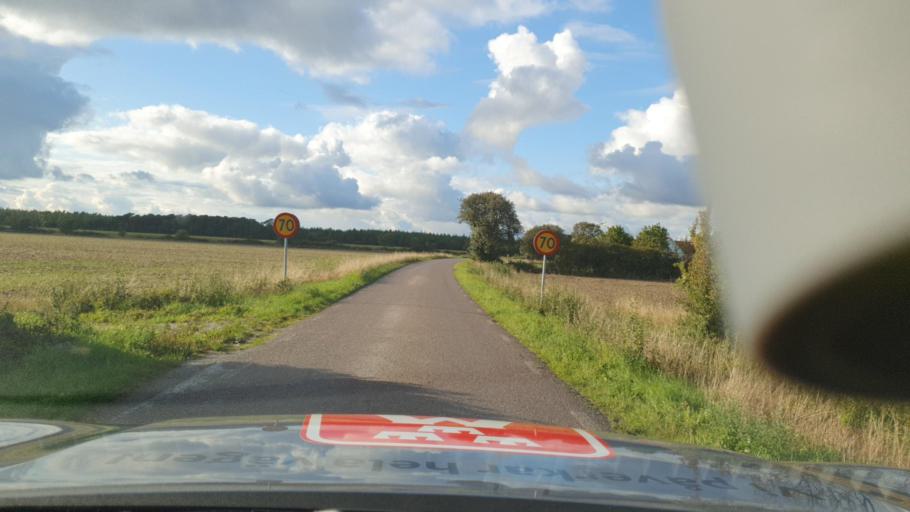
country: SE
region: Gotland
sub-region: Gotland
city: Hemse
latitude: 57.1890
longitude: 18.2587
